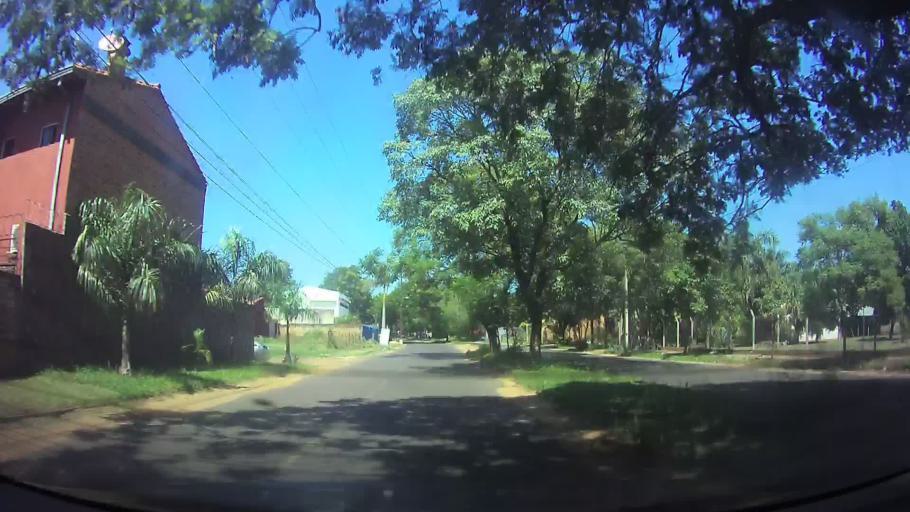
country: PY
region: Central
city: Fernando de la Mora
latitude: -25.2910
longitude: -57.5216
